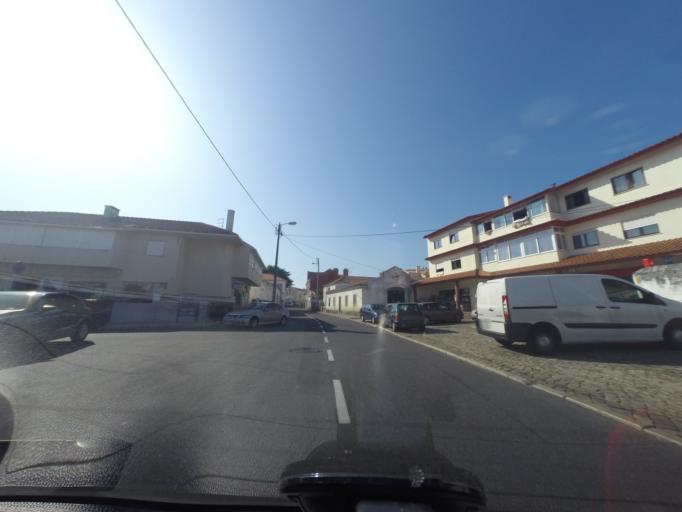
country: PT
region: Lisbon
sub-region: Cascais
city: Alcabideche
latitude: 38.7316
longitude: -9.4086
